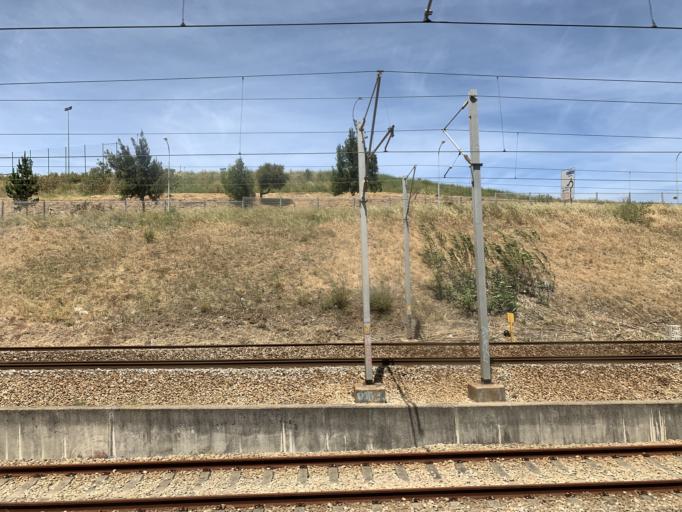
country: PT
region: Lisbon
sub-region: Sintra
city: Queluz
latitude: 38.7514
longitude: -9.2673
